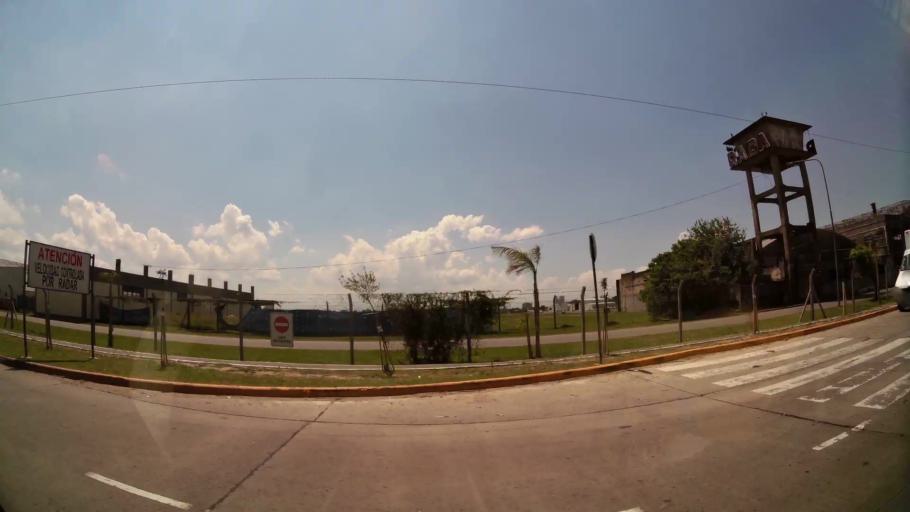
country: AR
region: Buenos Aires
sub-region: Partido de Tigre
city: Tigre
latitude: -34.4547
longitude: -58.5799
